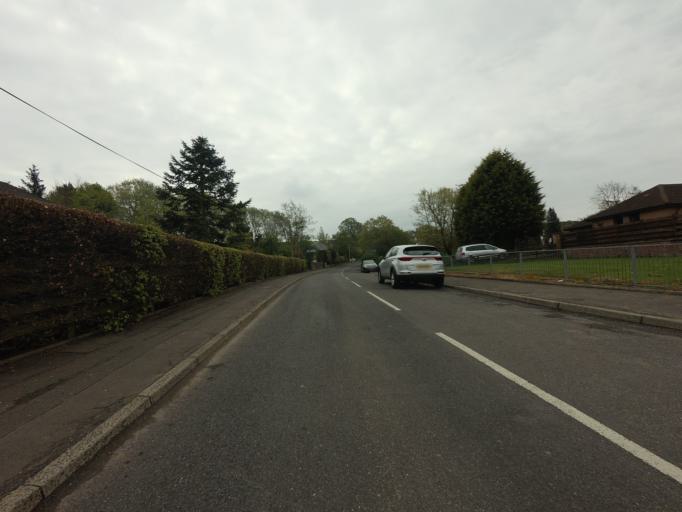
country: GB
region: Scotland
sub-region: Falkirk
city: Polmont
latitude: 55.9799
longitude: -3.7377
